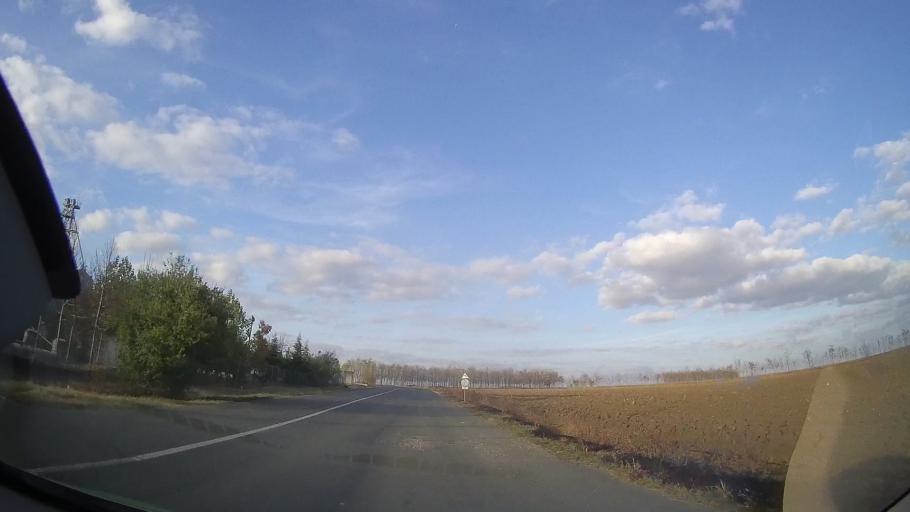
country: RO
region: Constanta
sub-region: Comuna Dumbraveni
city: Dumbraveni
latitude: 43.9268
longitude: 28.0297
